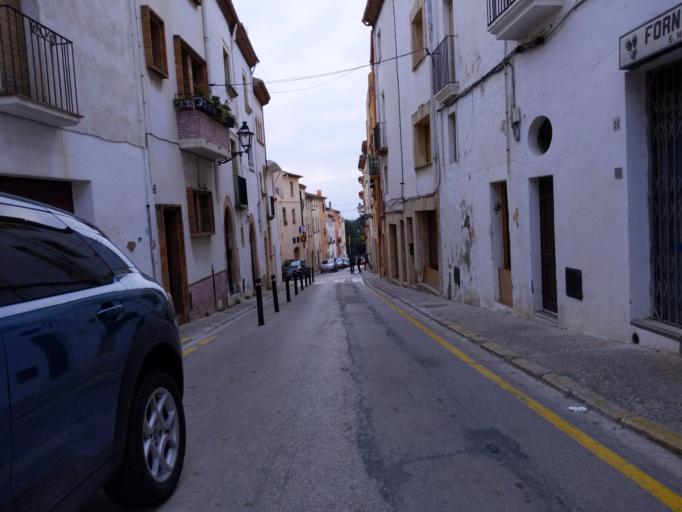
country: ES
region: Catalonia
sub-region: Provincia de Tarragona
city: Altafulla
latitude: 41.1412
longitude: 1.3751
